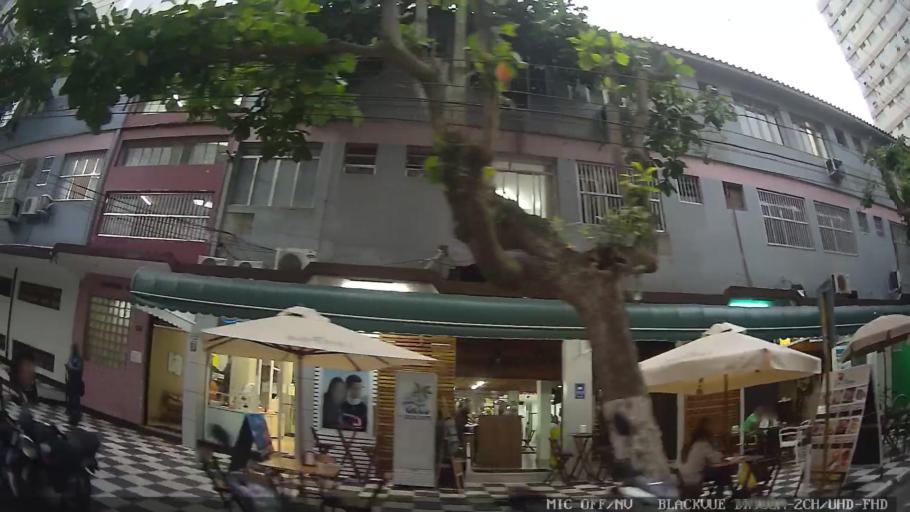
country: BR
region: Sao Paulo
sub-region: Guaruja
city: Guaruja
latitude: -23.9942
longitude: -46.2545
